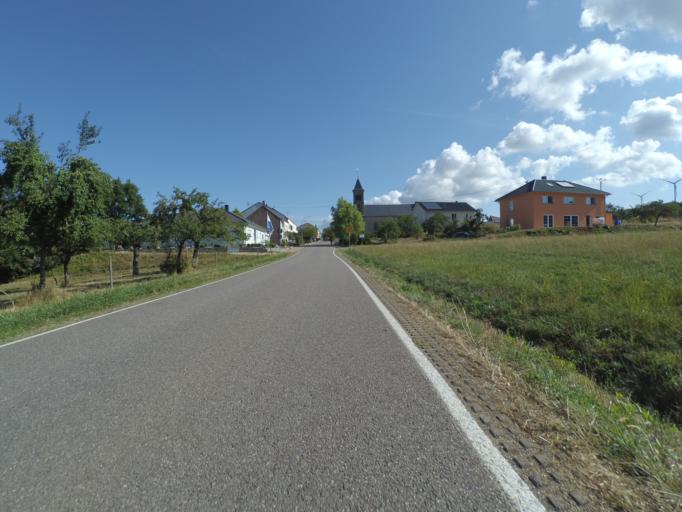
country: DE
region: Saarland
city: Perl
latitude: 49.5131
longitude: 6.4138
